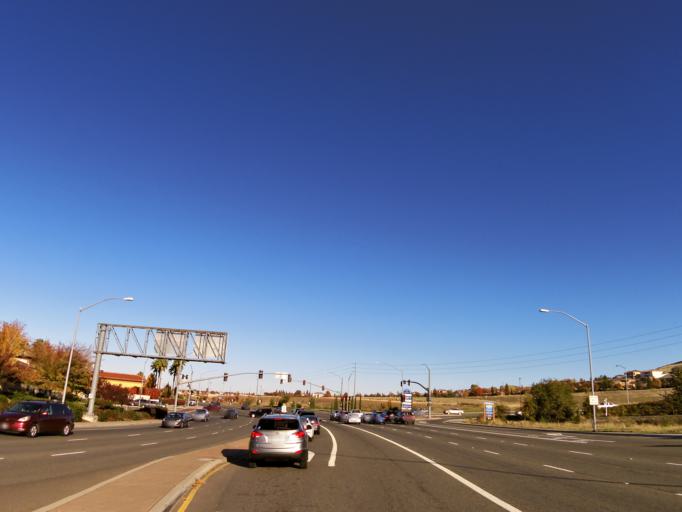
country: US
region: California
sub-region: El Dorado County
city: El Dorado Hills
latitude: 38.6471
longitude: -121.1150
